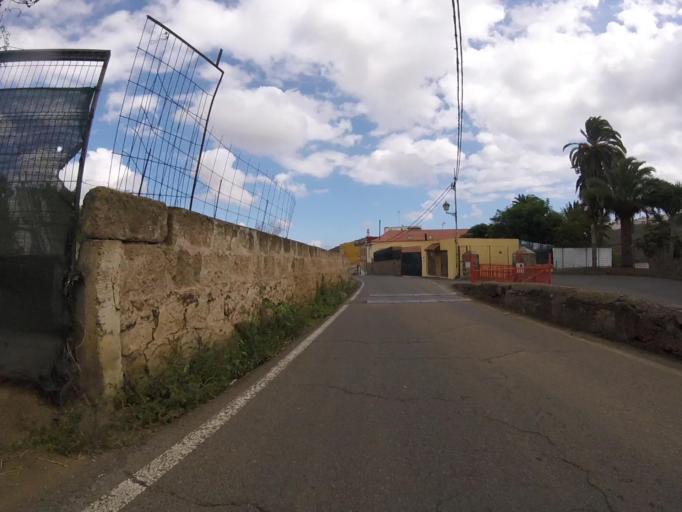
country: ES
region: Canary Islands
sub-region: Provincia de Las Palmas
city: Santa Brigida
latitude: 28.0462
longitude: -15.4845
